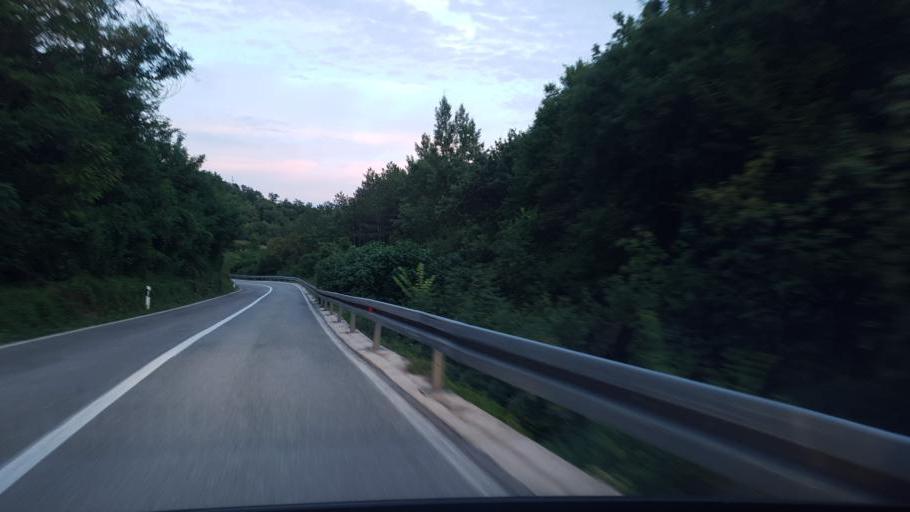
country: HR
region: Primorsko-Goranska
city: Punat
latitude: 45.0149
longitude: 14.6976
